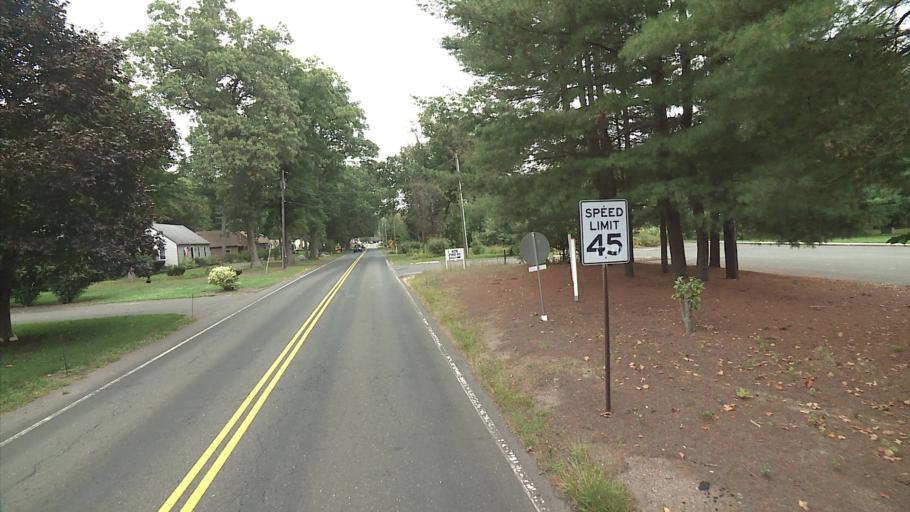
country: US
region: Connecticut
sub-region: Hartford County
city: Suffield Depot
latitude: 42.0363
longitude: -72.6859
